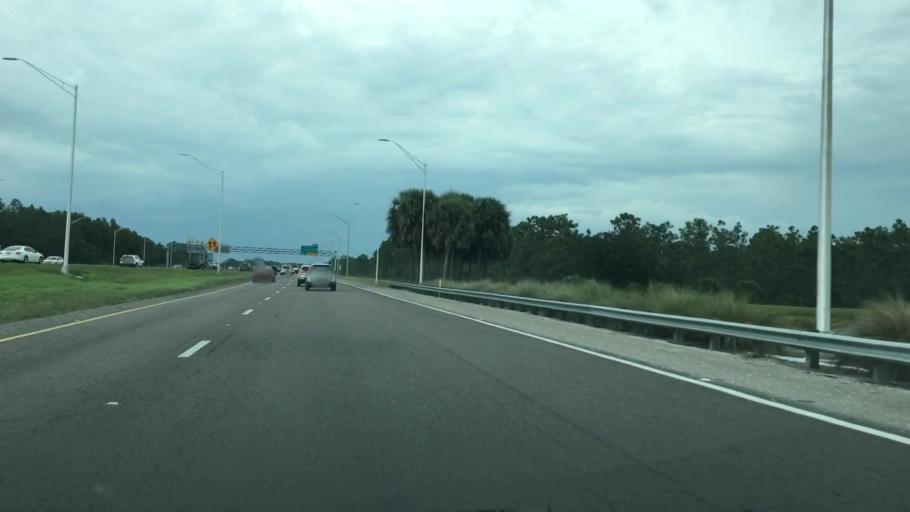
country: US
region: Florida
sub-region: Orange County
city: Alafaya
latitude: 28.4580
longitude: -81.2307
